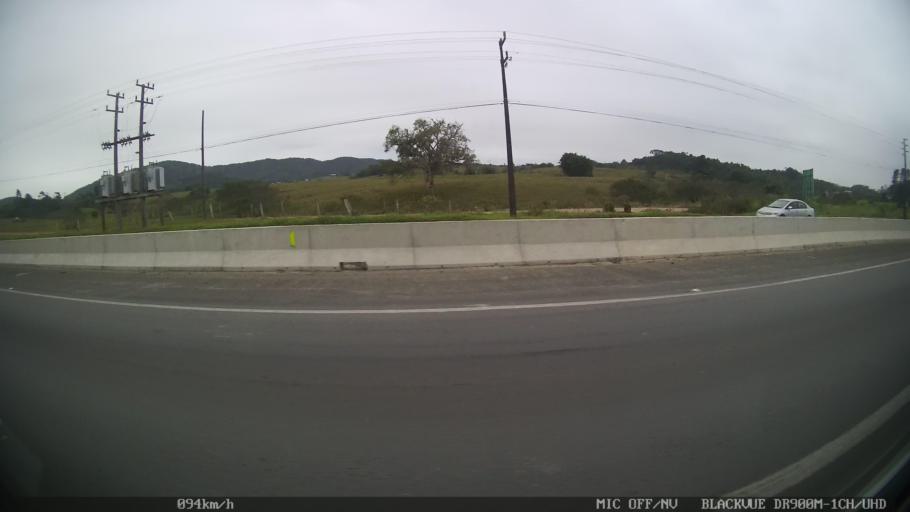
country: BR
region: Santa Catarina
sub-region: Barra Velha
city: Barra Velha
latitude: -26.6830
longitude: -48.6944
